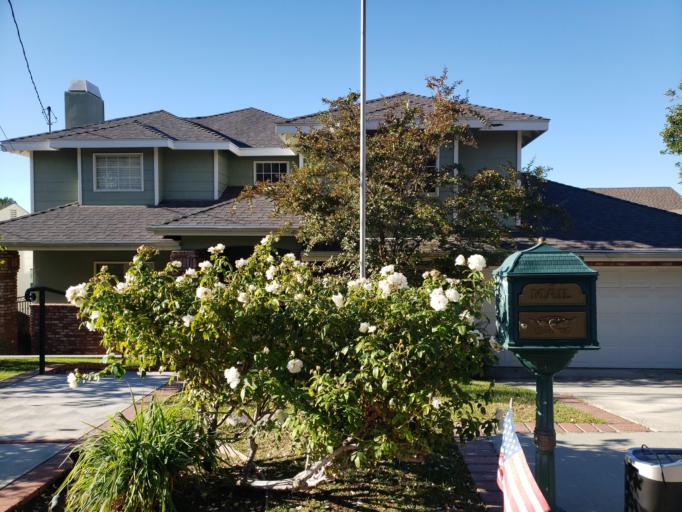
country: US
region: California
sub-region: Los Angeles County
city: La Crescenta-Montrose
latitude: 34.2339
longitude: -118.2382
